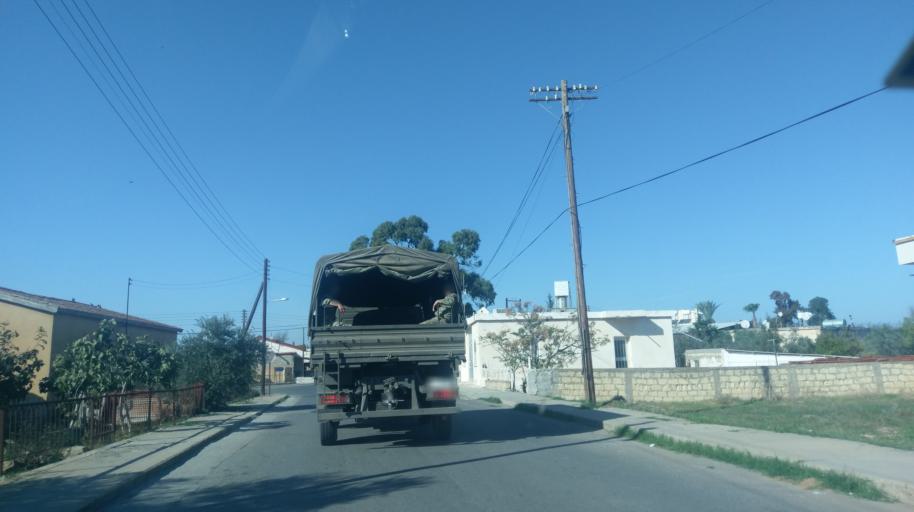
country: CY
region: Ammochostos
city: Famagusta
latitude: 35.1030
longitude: 33.9472
